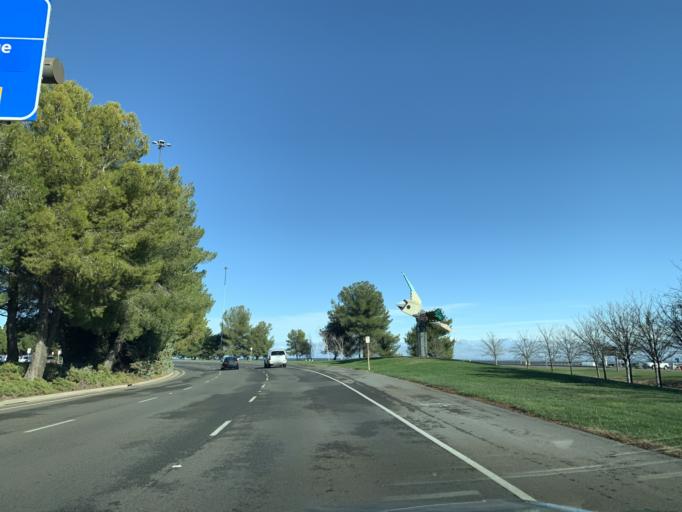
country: US
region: California
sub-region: Yolo County
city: West Sacramento
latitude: 38.6864
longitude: -121.5880
